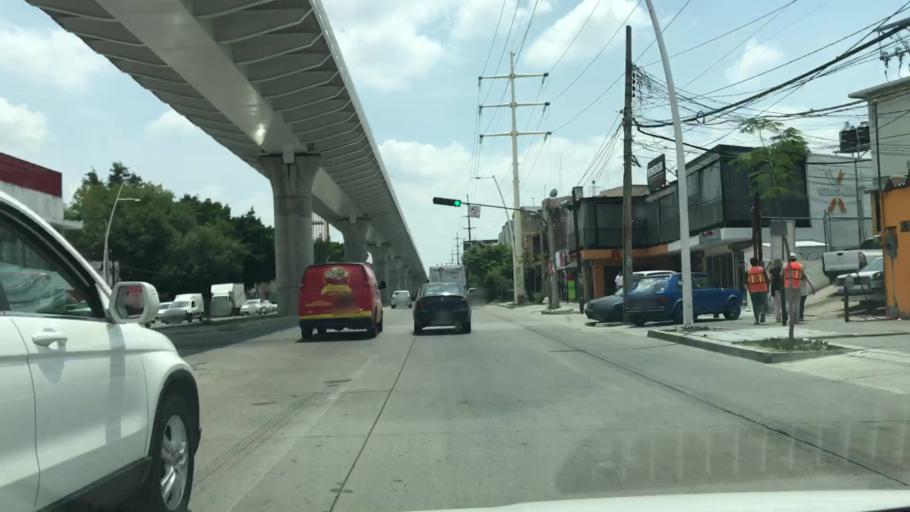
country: MX
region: Jalisco
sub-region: Zapopan
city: Zapopan
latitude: 20.7046
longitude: -103.3631
